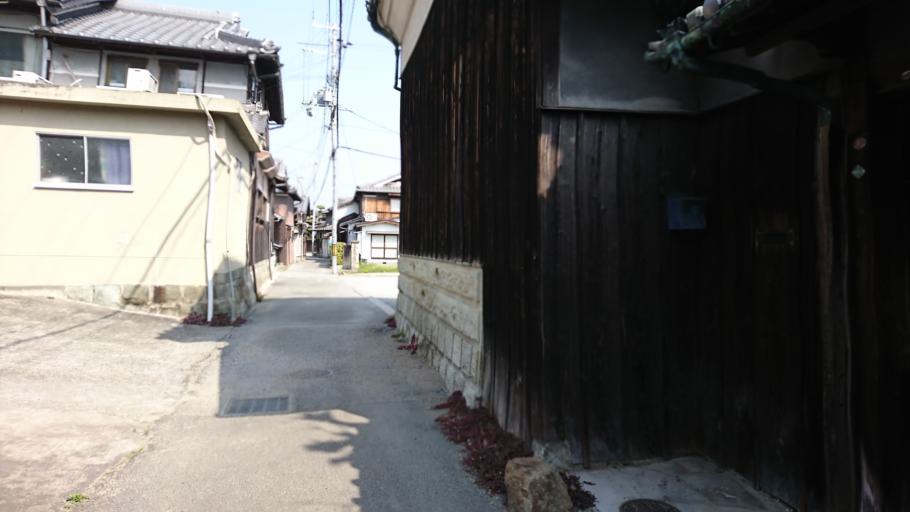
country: JP
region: Hyogo
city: Shirahamacho-usazakiminami
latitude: 34.7913
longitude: 134.7631
